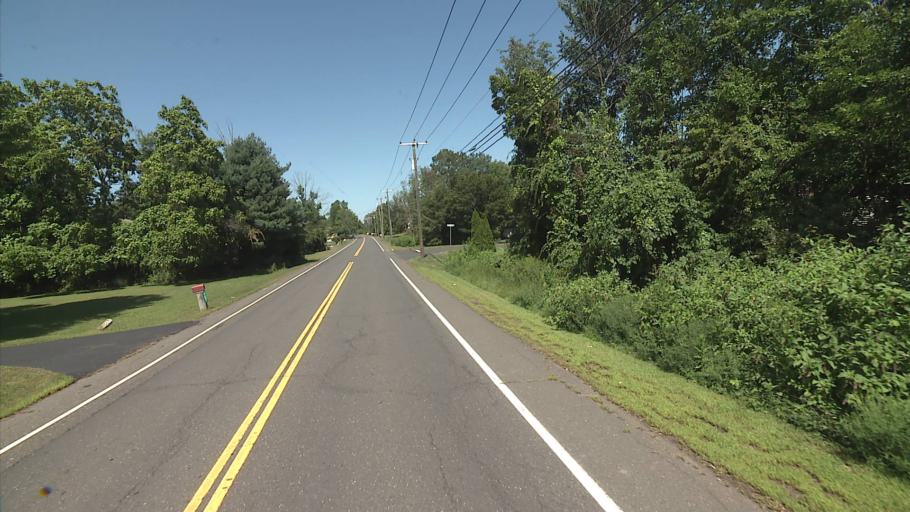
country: US
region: Connecticut
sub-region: Hartford County
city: Enfield
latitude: 41.9730
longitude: -72.6142
